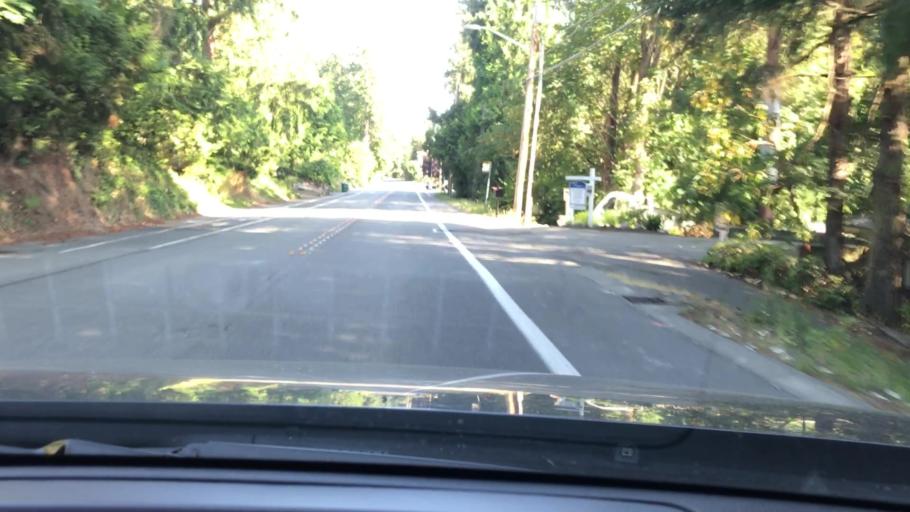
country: US
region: Washington
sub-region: King County
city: Sammamish
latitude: 47.6343
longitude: -122.0914
